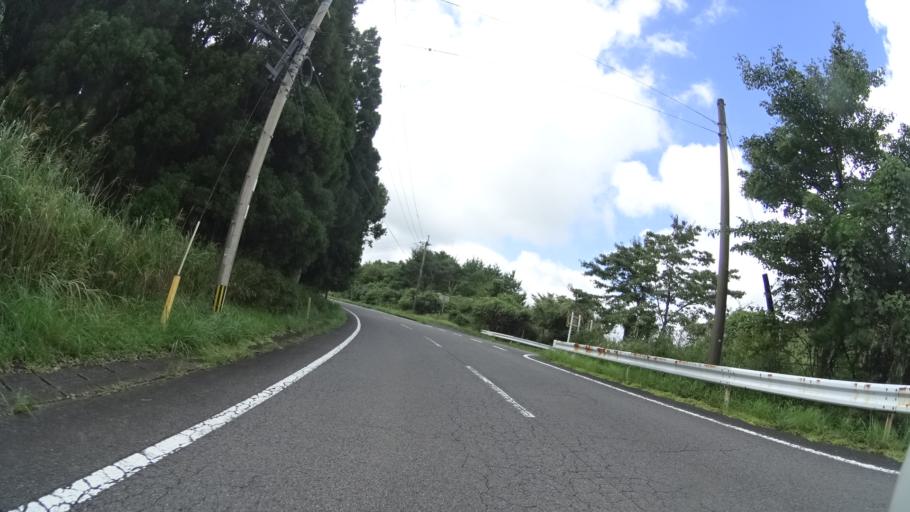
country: JP
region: Oita
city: Beppu
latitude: 33.3217
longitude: 131.4142
